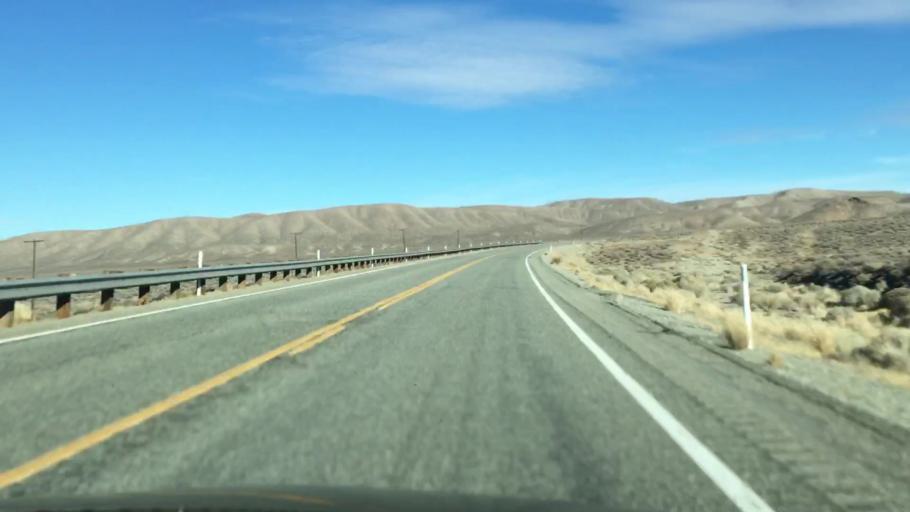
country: US
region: Nevada
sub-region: Lyon County
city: Yerington
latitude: 39.0446
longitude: -118.9791
